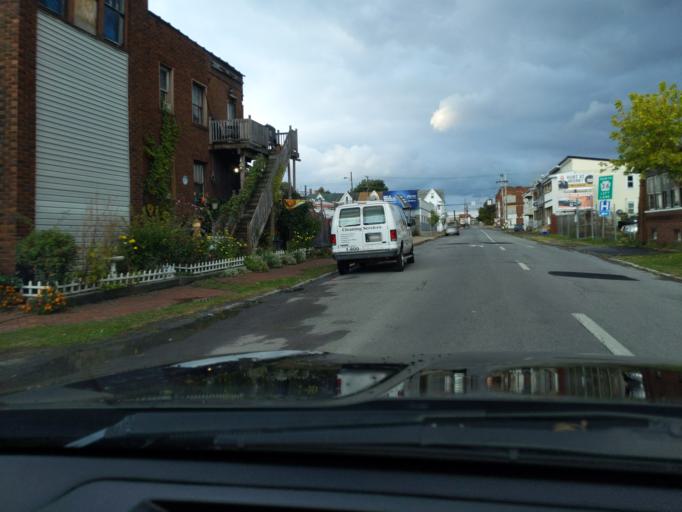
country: US
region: Pennsylvania
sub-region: Blair County
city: Altoona
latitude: 40.5054
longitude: -78.4082
